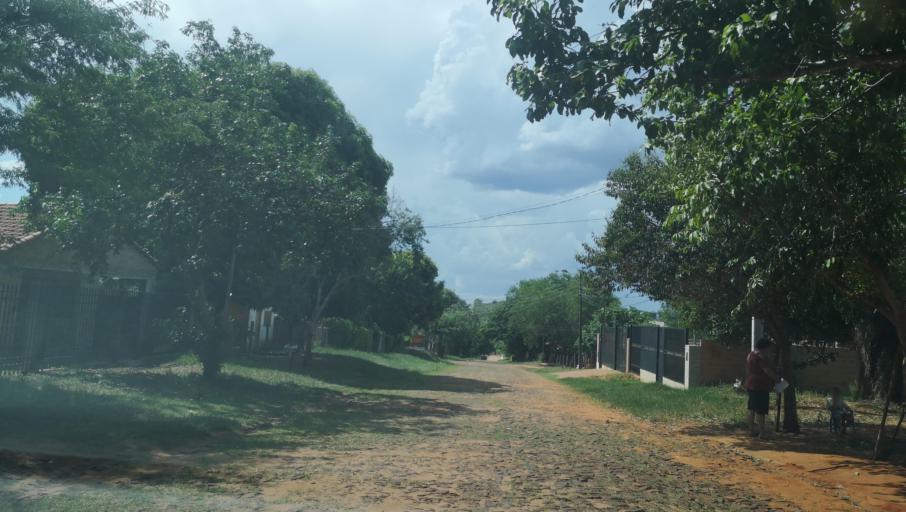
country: PY
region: Misiones
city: Santa Maria
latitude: -26.8882
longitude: -57.0143
